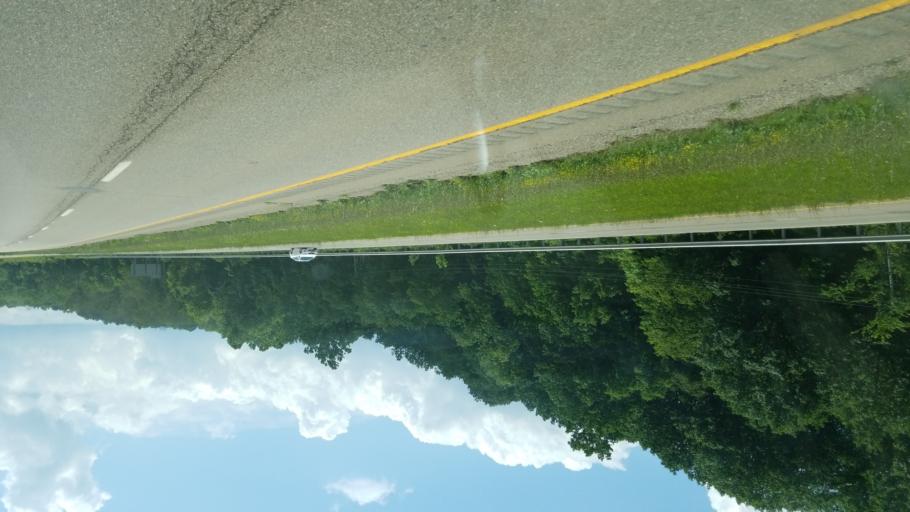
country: US
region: Ohio
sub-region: Tuscarawas County
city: New Philadelphia
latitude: 40.4777
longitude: -81.4843
